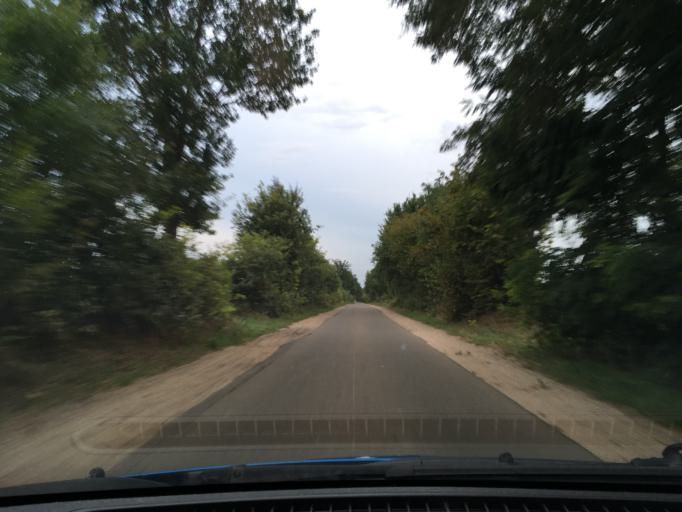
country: DE
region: Schleswig-Holstein
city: Lanze
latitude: 53.3987
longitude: 10.6059
